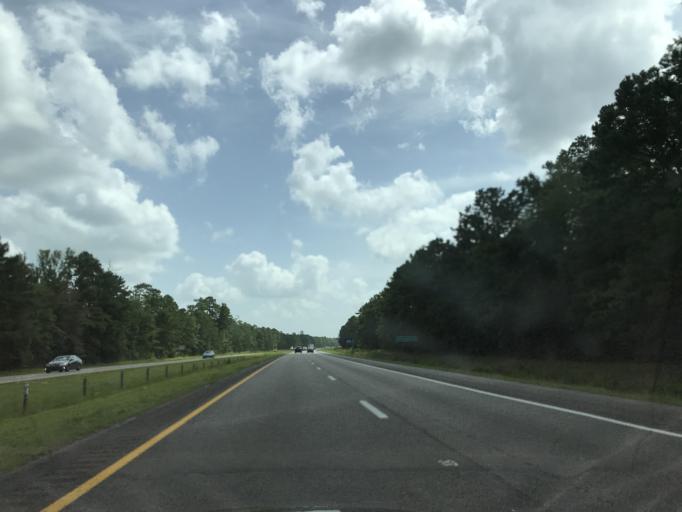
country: US
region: North Carolina
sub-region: Pender County
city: Burgaw
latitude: 34.5548
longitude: -77.8944
